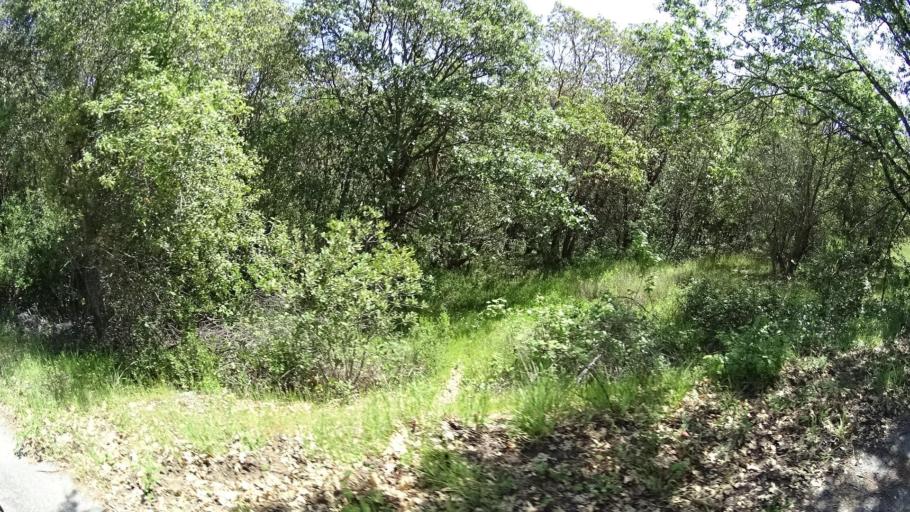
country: US
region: California
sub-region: Humboldt County
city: Redway
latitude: 40.1657
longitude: -123.6032
